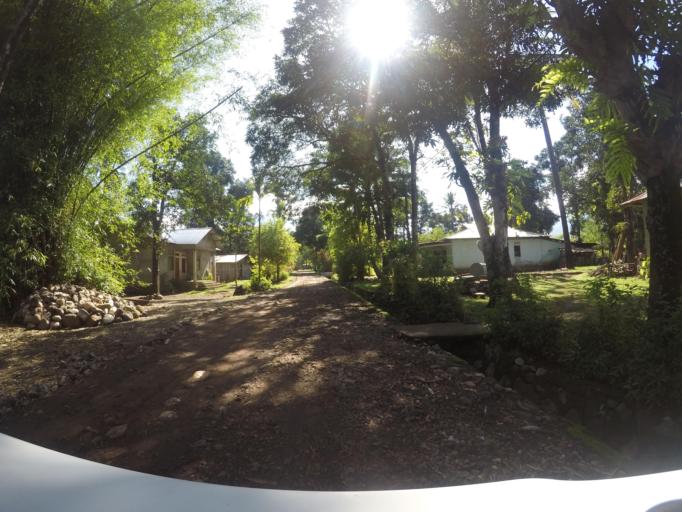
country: TL
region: Bobonaro
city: Maliana
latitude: -8.9908
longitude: 125.2059
